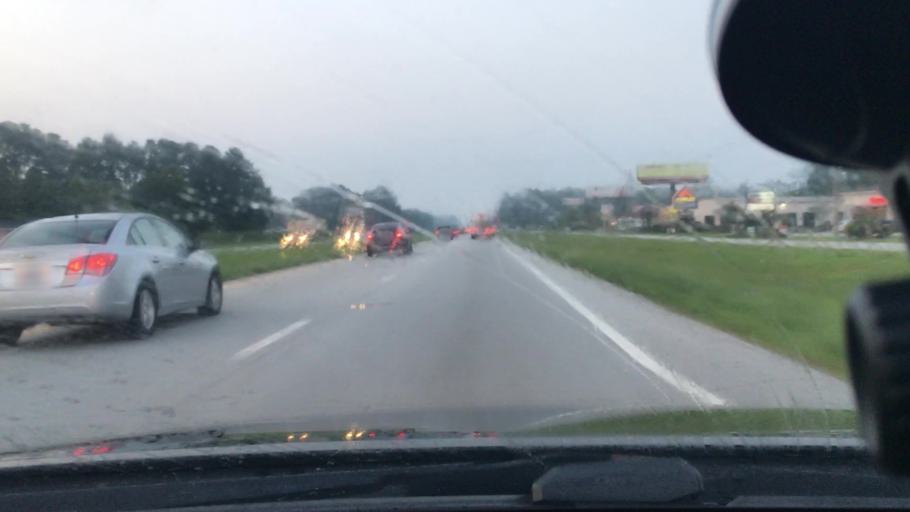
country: US
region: North Carolina
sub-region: Craven County
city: James City
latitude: 35.0604
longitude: -77.0201
